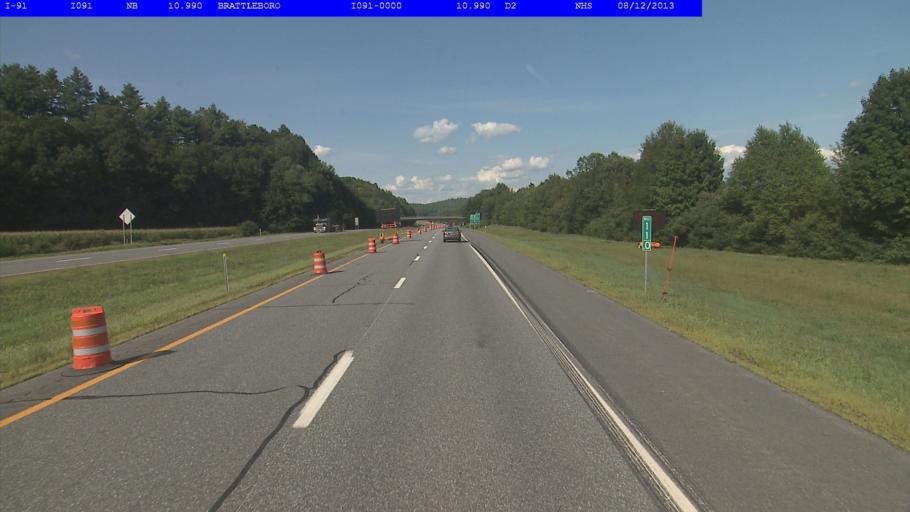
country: US
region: Vermont
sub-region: Windham County
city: Brattleboro
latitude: 42.8790
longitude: -72.5652
